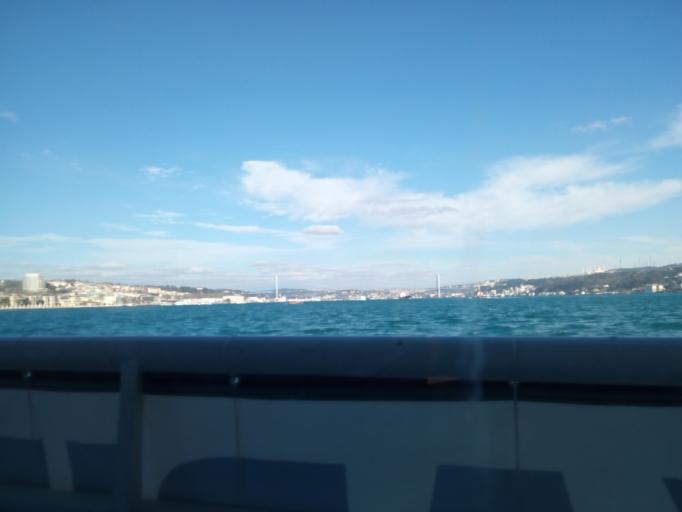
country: TR
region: Istanbul
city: Eminoenue
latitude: 41.0320
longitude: 28.9959
